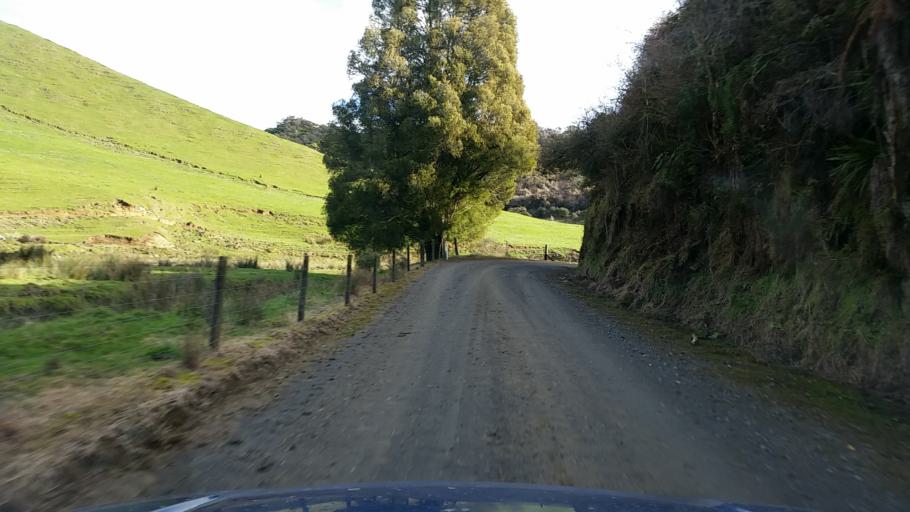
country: NZ
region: Taranaki
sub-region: South Taranaki District
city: Eltham
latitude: -39.2613
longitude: 174.5822
